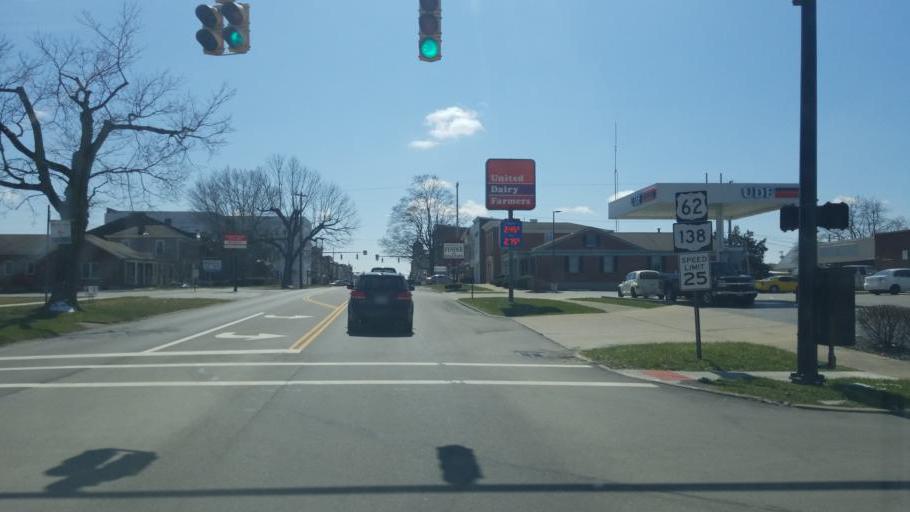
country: US
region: Ohio
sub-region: Highland County
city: Hillsboro
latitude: 39.2049
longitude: -83.6109
